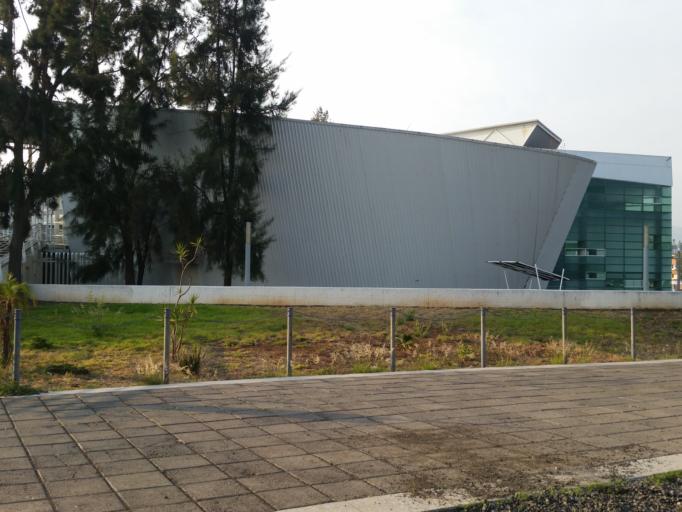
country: MX
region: Michoacan
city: Morelia
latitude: 19.6880
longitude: -101.2036
